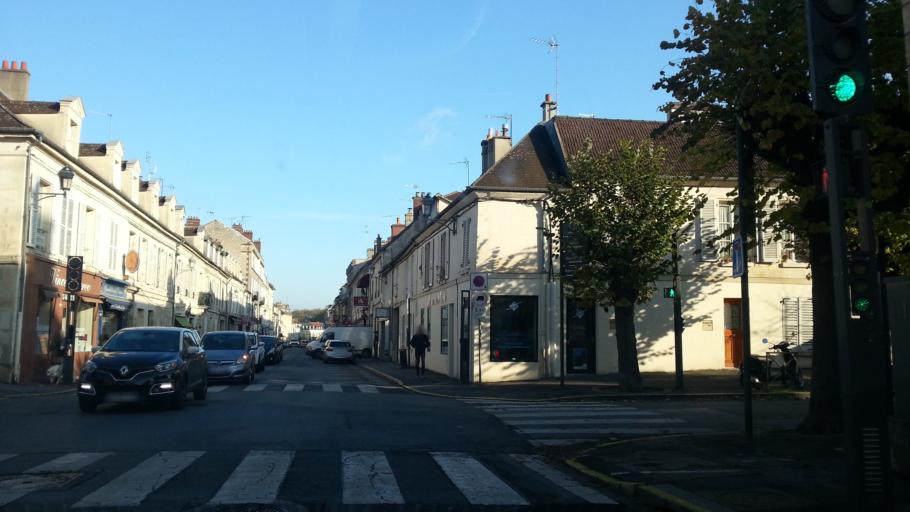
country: FR
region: Picardie
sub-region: Departement de l'Oise
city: Chantilly
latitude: 49.1944
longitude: 2.4725
